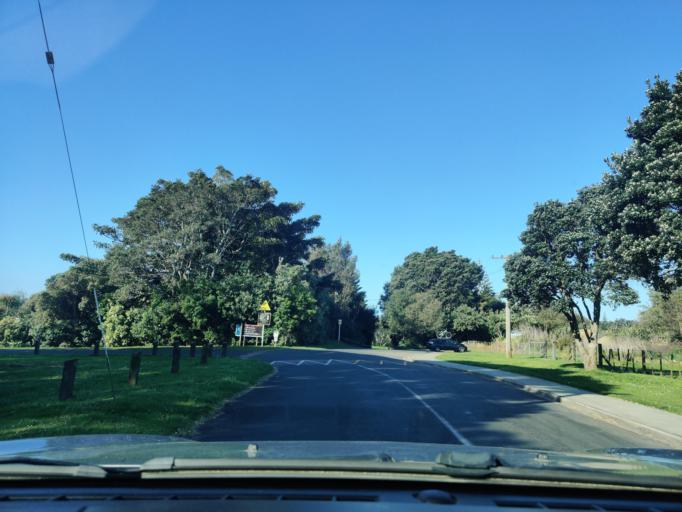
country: NZ
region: Taranaki
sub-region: New Plymouth District
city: New Plymouth
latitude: -39.0434
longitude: 174.1139
